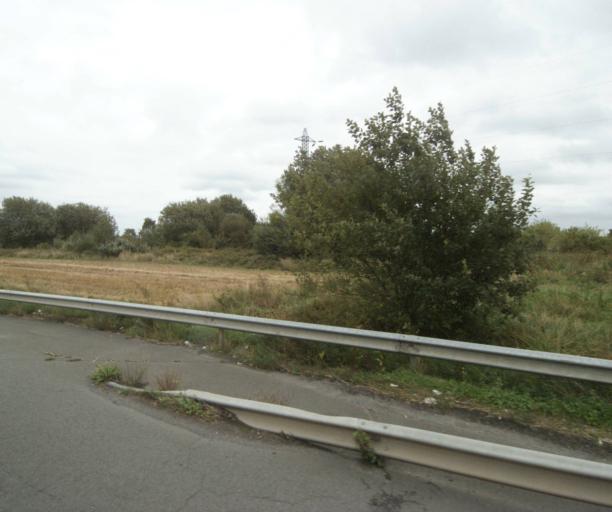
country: FR
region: Nord-Pas-de-Calais
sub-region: Departement du Nord
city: Hallennes-lez-Haubourdin
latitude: 50.6192
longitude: 2.9580
